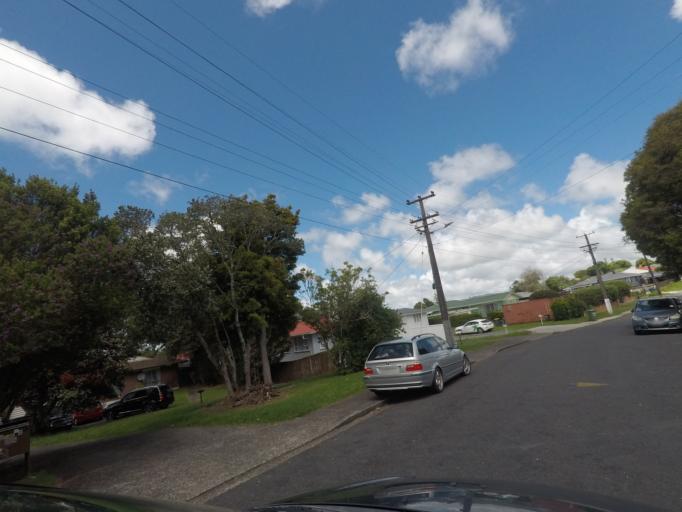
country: NZ
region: Auckland
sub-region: Auckland
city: Rosebank
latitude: -36.8715
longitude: 174.6488
